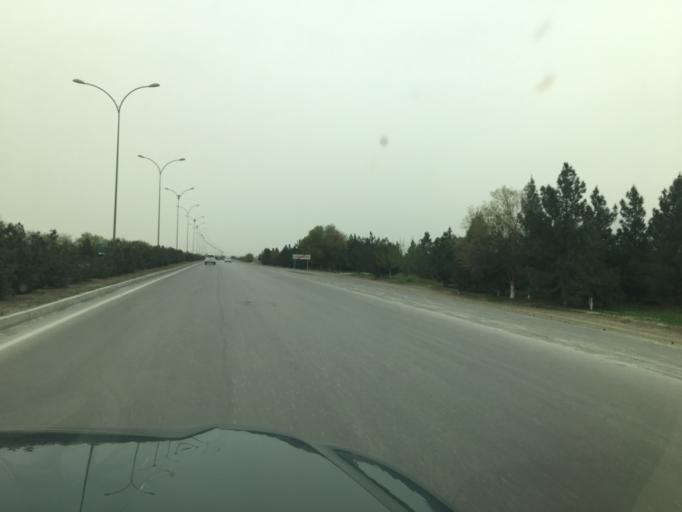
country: TM
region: Ahal
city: Abadan
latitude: 38.1441
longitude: 57.9935
